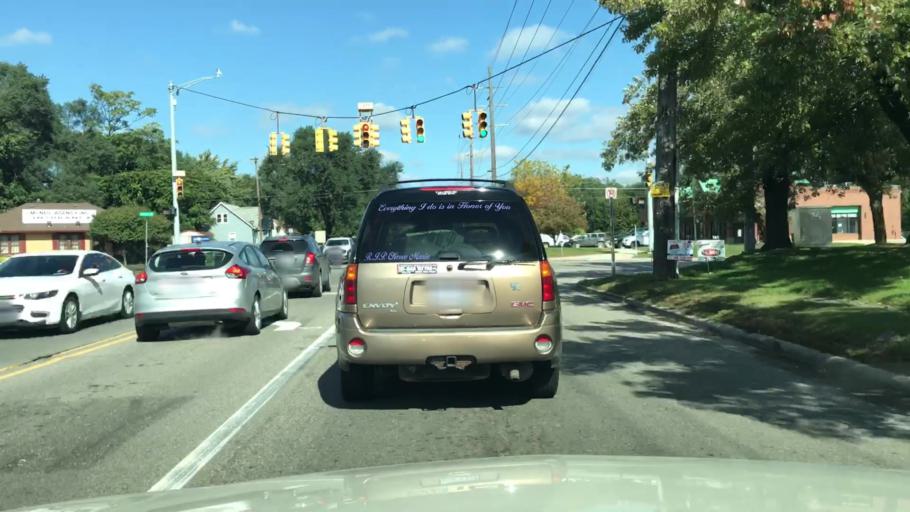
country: US
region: Michigan
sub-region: Oakland County
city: Rochester
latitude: 42.6384
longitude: -83.0921
